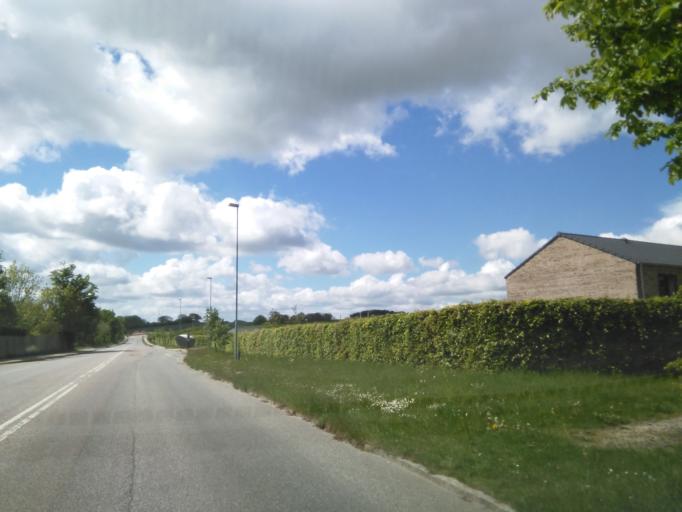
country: DK
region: Central Jutland
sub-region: Arhus Kommune
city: Malling
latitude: 56.0323
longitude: 10.1873
